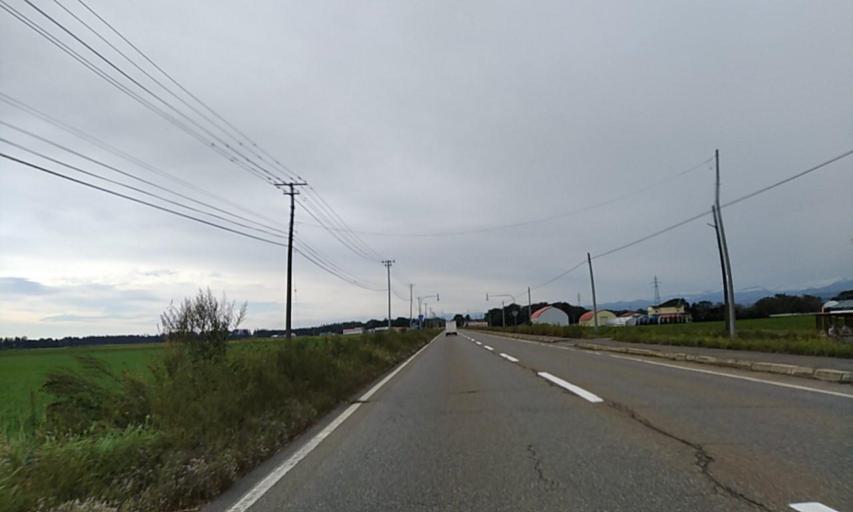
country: JP
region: Hokkaido
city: Obihiro
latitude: 42.7769
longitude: 143.1573
